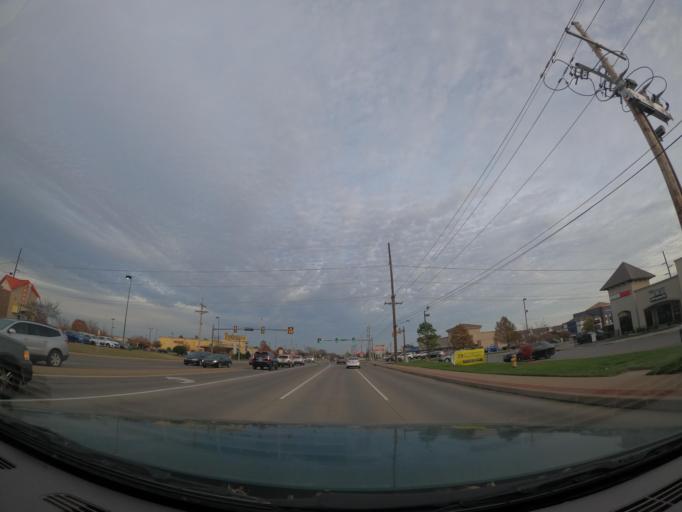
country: US
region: Oklahoma
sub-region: Tulsa County
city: Broken Arrow
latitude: 36.0608
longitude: -95.8558
